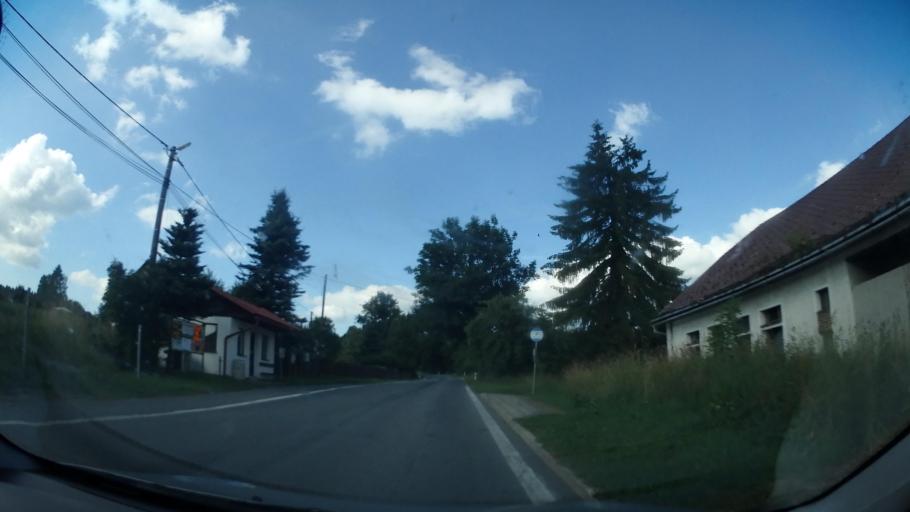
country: CZ
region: Vysocina
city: Heralec
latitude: 49.6454
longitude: 15.9678
